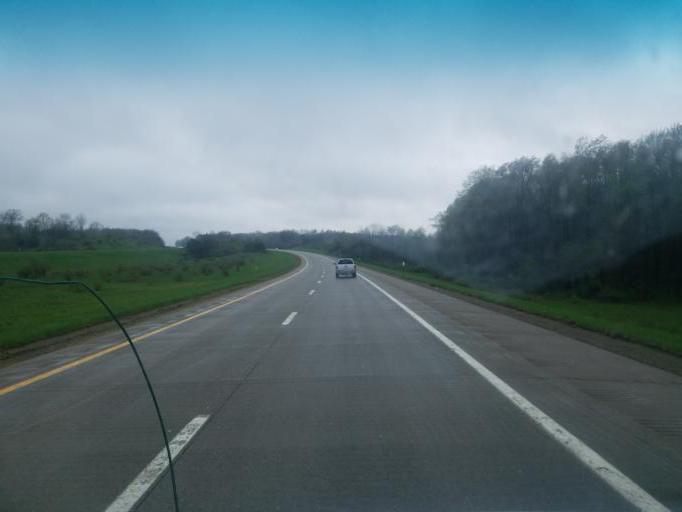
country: US
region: New York
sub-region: Chautauqua County
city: Clymer
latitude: 42.1481
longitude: -79.6552
